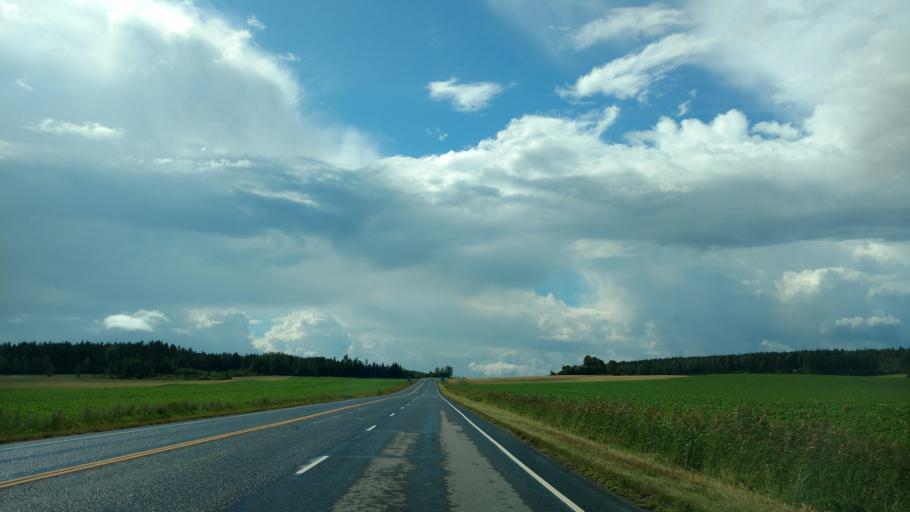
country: FI
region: Varsinais-Suomi
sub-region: Salo
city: Halikko
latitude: 60.3757
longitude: 22.9839
